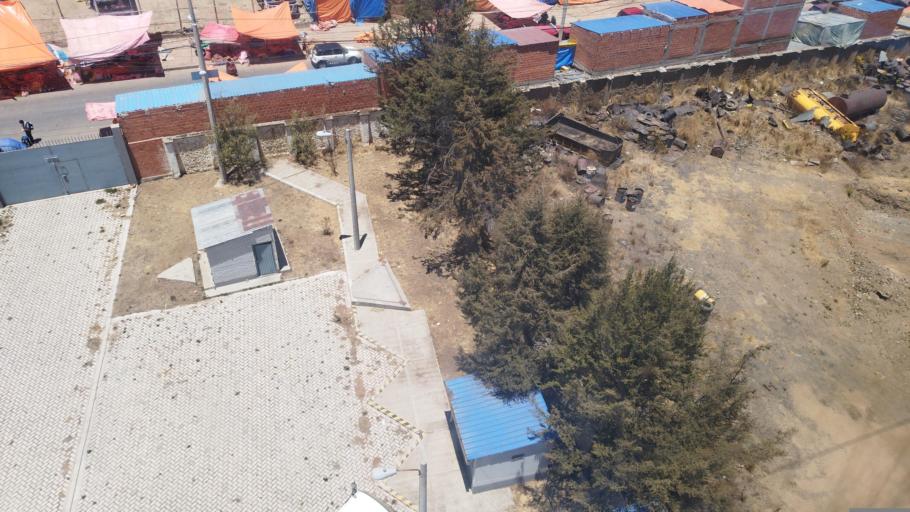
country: BO
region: La Paz
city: La Paz
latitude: -16.5074
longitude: -68.1576
